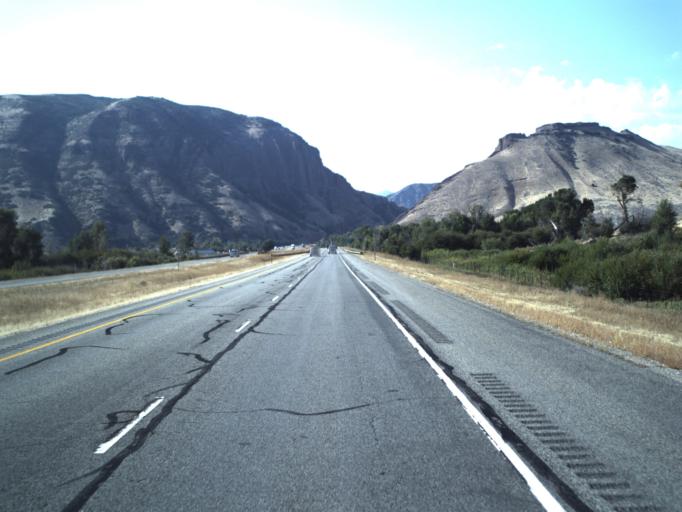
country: US
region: Utah
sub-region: Summit County
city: Coalville
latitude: 41.0340
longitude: -111.5071
